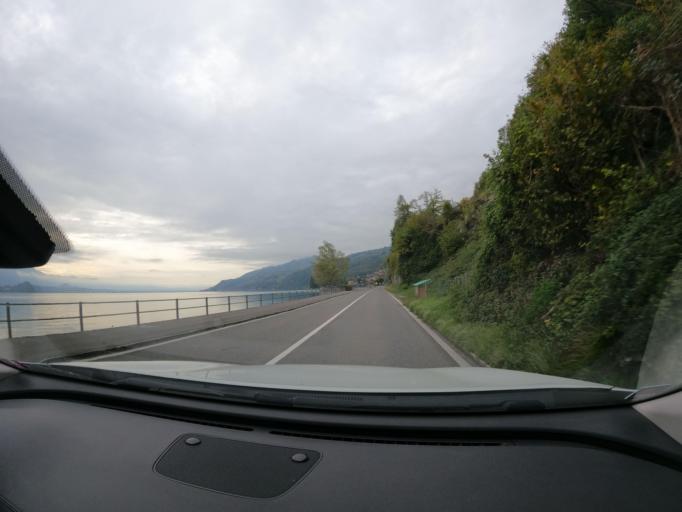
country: CH
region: Bern
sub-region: Thun District
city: Sigriswil
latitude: 46.6882
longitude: 7.7440
